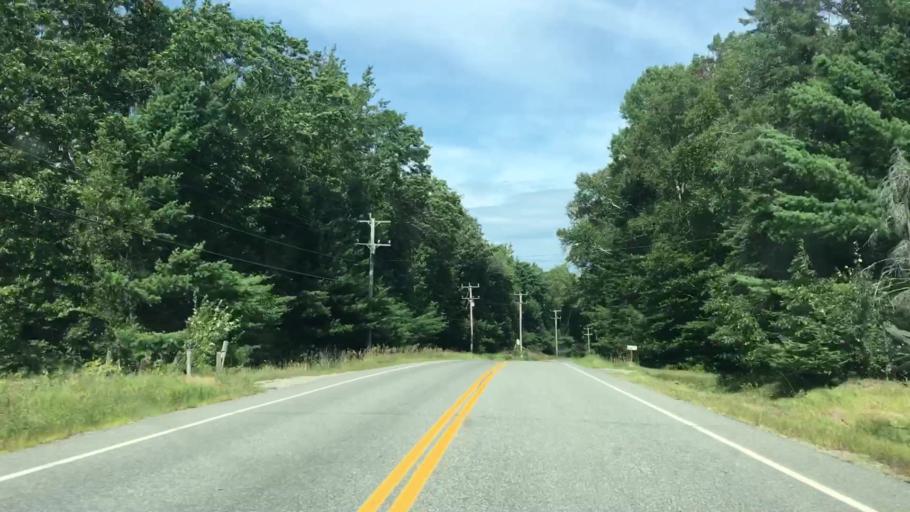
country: US
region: Maine
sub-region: Penobscot County
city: Lincoln
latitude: 45.4004
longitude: -68.5088
